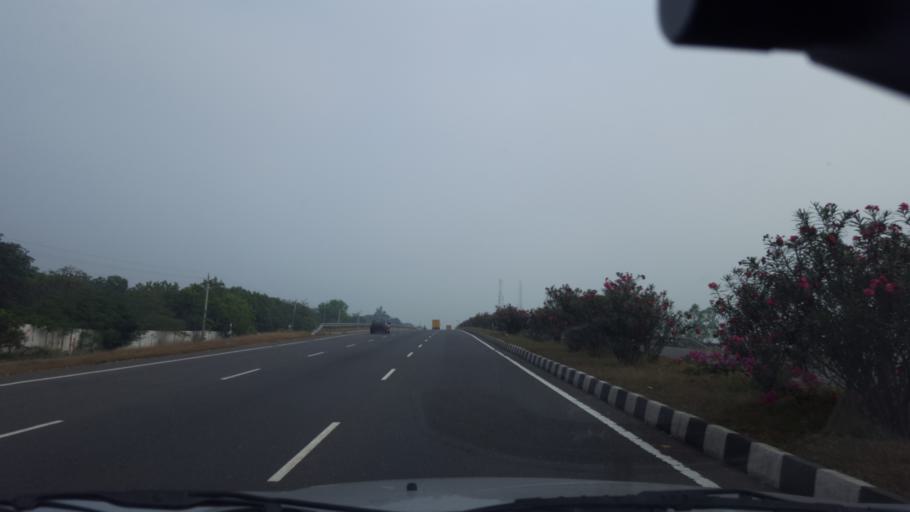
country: IN
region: Andhra Pradesh
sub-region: Guntur
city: Chilakalurupet
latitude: 16.0433
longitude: 80.1377
